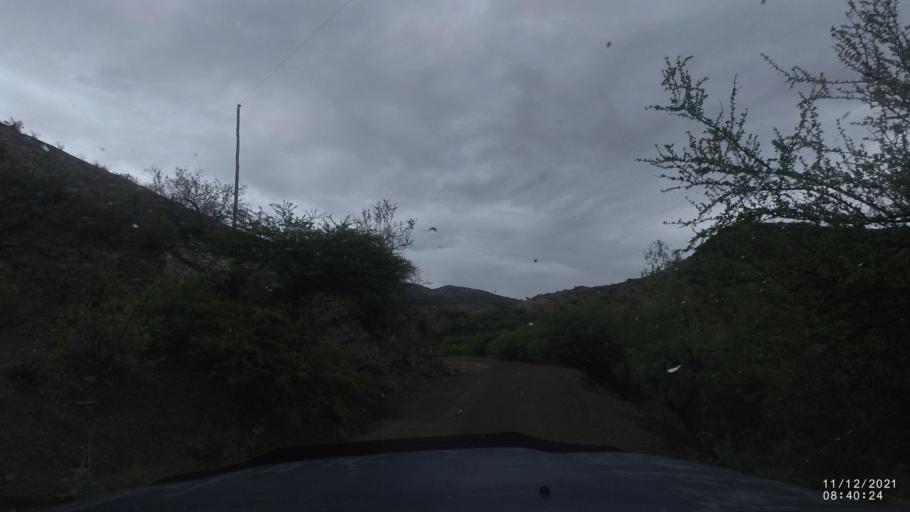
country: BO
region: Cochabamba
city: Tarata
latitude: -17.9188
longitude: -65.9343
